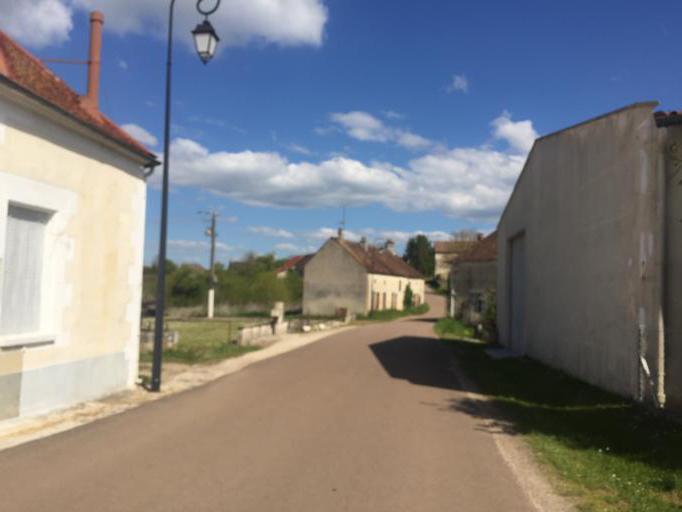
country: FR
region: Bourgogne
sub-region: Departement de l'Yonne
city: Fontenailles
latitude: 47.5598
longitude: 3.3256
